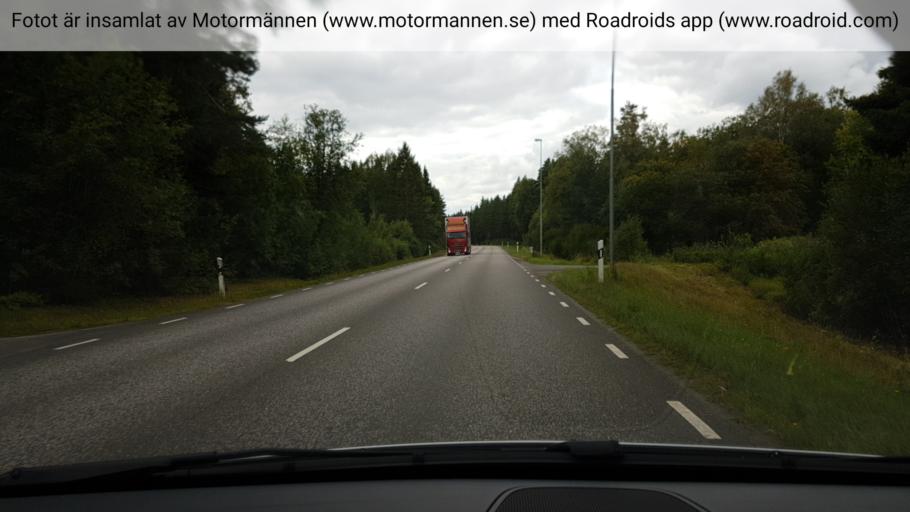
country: SE
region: Vaestra Goetaland
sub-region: Tidaholms Kommun
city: Tidaholm
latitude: 58.1926
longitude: 13.9362
